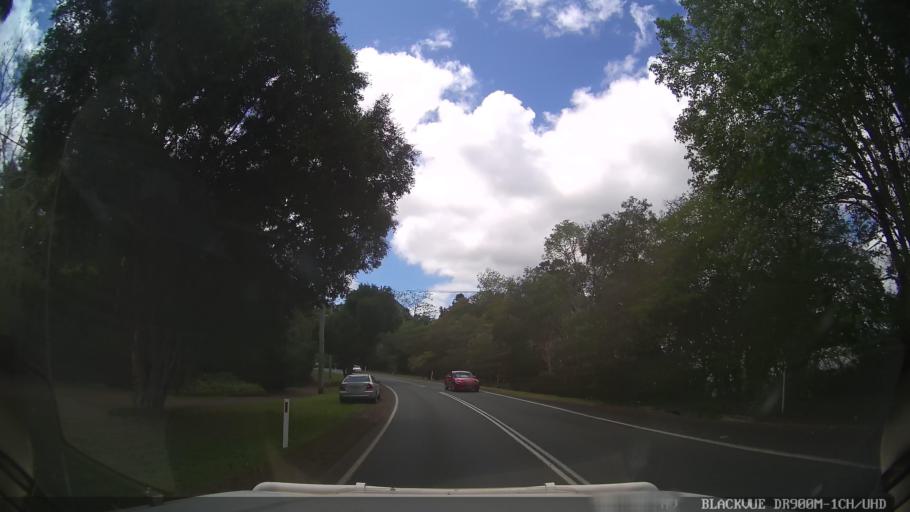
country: AU
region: Queensland
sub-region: Sunshine Coast
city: Nambour
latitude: -26.6629
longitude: 152.8813
